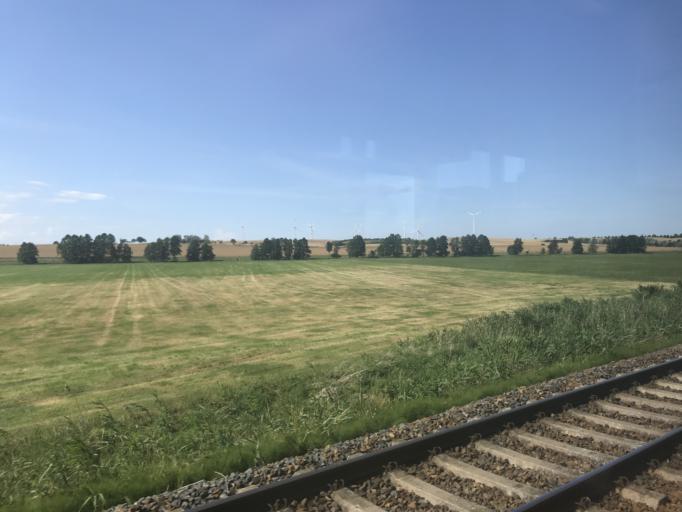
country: DE
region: Brandenburg
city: Passow
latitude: 53.1387
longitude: 14.0859
